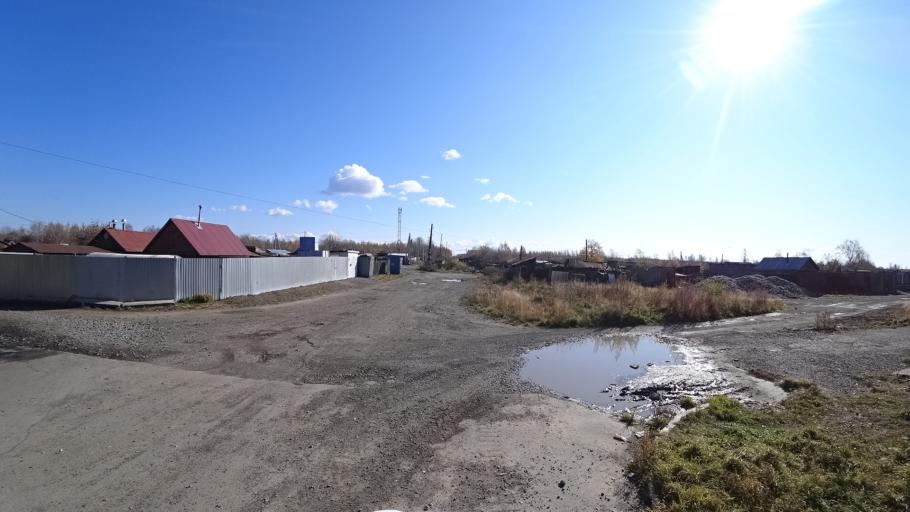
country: RU
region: Khabarovsk Krai
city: Amursk
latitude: 50.0989
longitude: 136.5172
